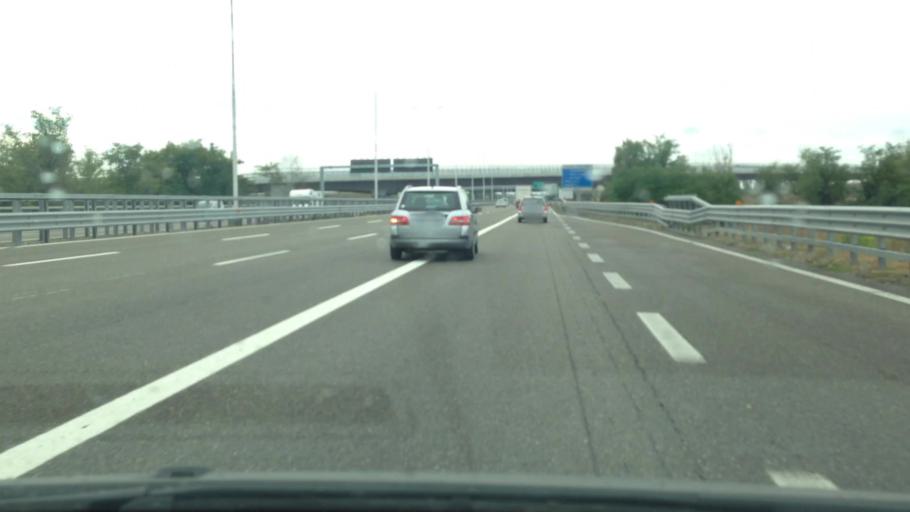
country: IT
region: Piedmont
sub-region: Provincia di Alessandria
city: Tortona
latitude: 44.9129
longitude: 8.8439
